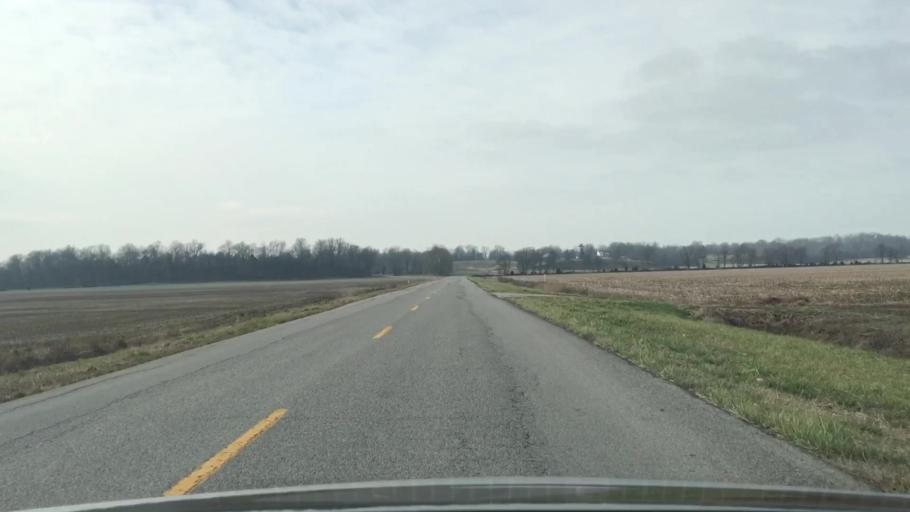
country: US
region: Kentucky
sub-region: McLean County
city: Calhoun
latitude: 37.5234
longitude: -87.3758
